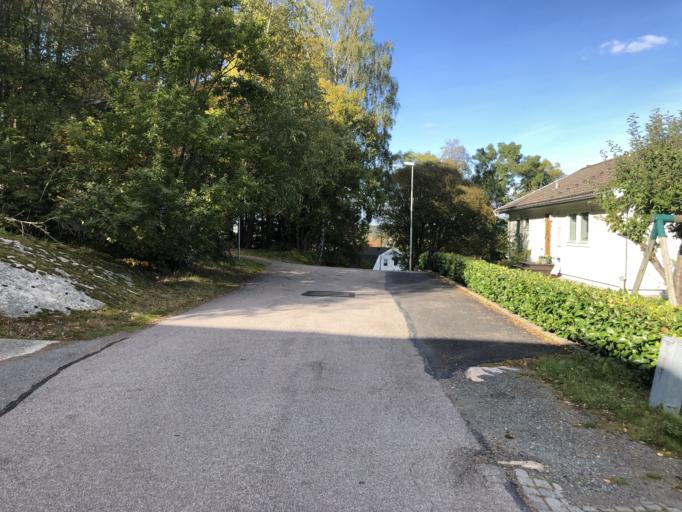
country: SE
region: Vaestra Goetaland
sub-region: Goteborg
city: Majorna
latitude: 57.6314
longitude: 11.9292
